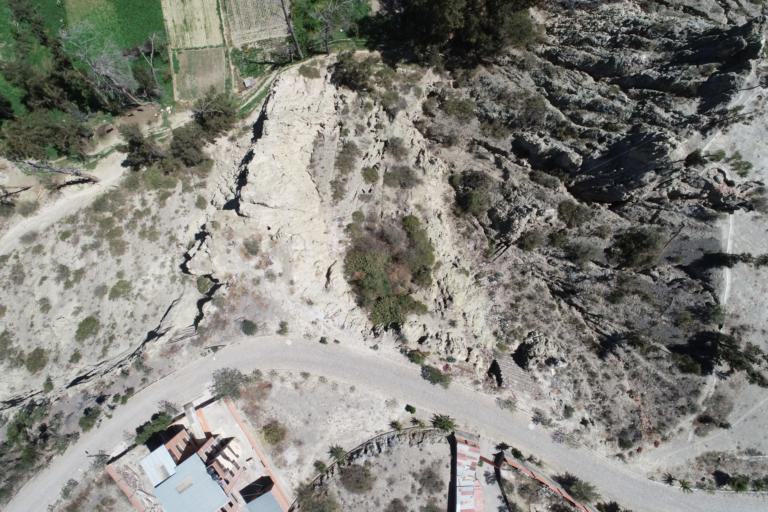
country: BO
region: La Paz
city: La Paz
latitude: -16.6300
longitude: -68.0572
